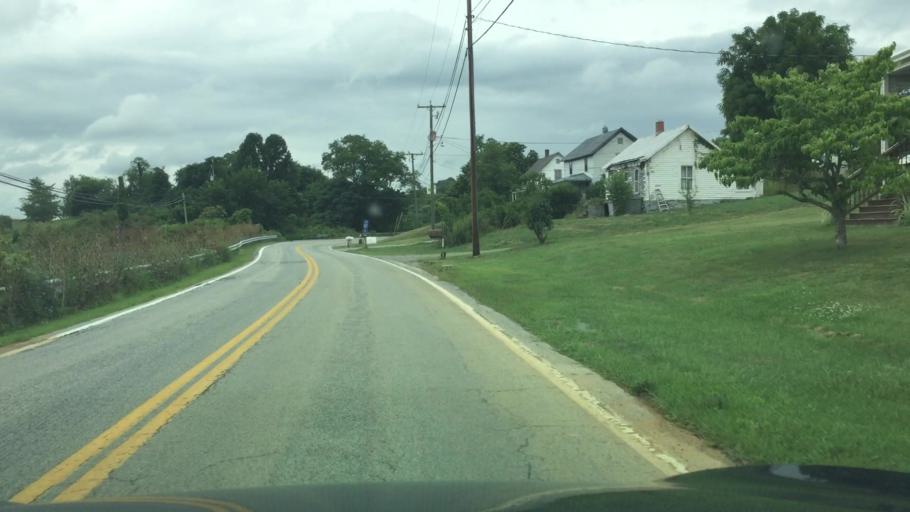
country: US
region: Virginia
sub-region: Pulaski County
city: Pulaski
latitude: 37.0057
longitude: -80.7487
